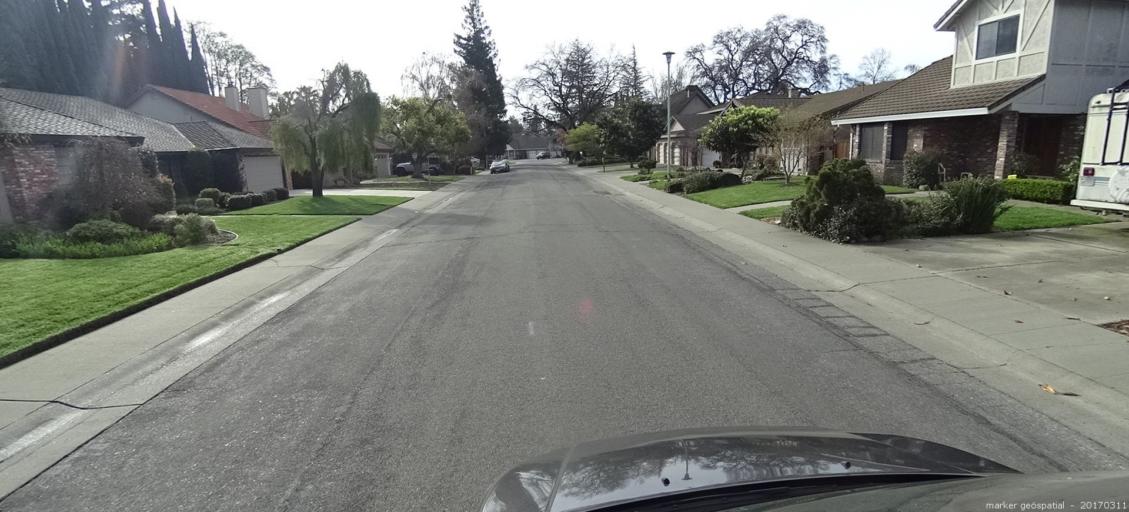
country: US
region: California
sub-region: Yolo County
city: West Sacramento
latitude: 38.5115
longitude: -121.5485
